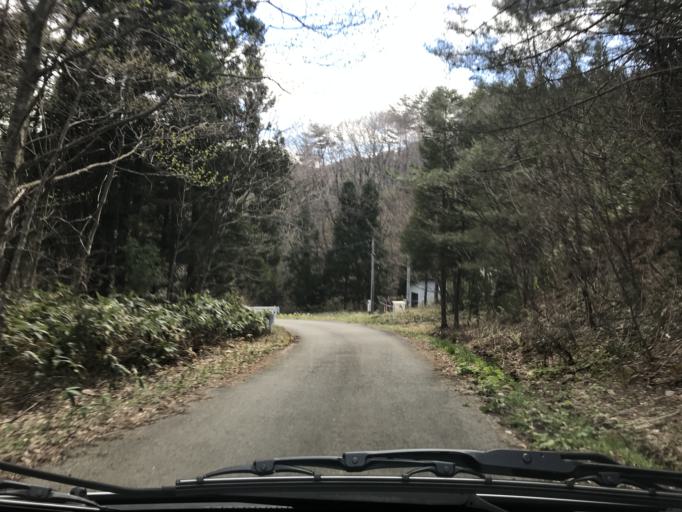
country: JP
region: Iwate
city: Mizusawa
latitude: 39.0767
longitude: 140.9888
